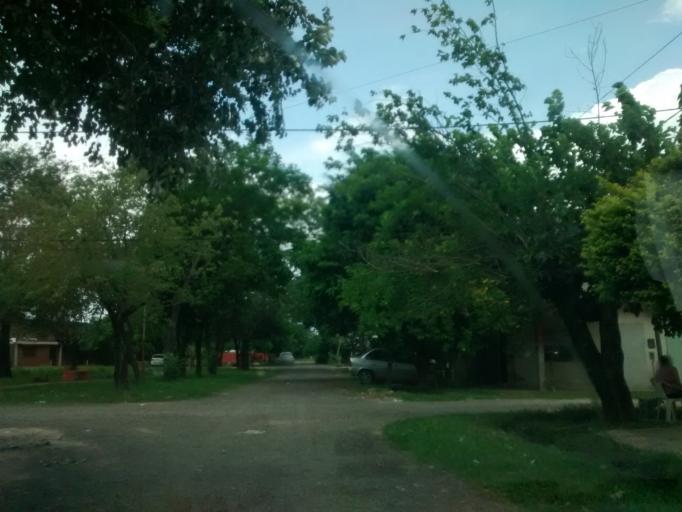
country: AR
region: Chaco
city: Resistencia
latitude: -27.4265
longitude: -58.9767
